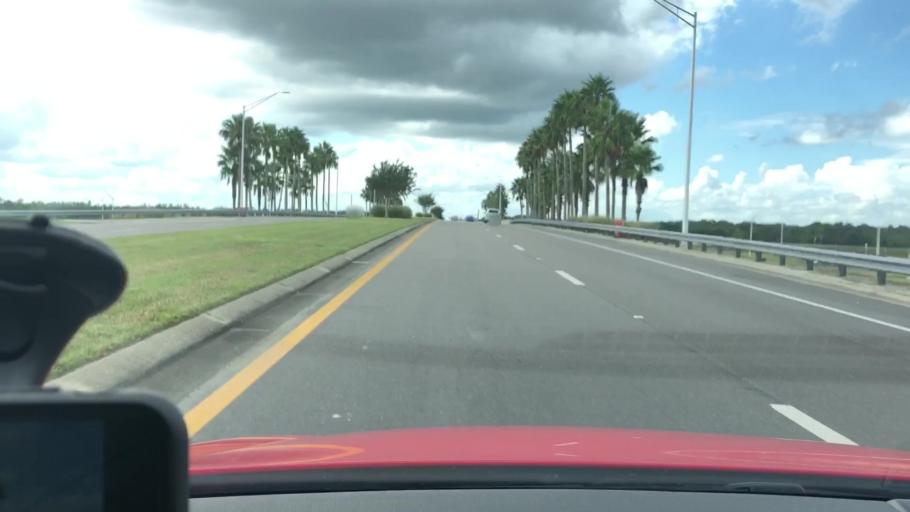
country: US
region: Florida
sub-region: Volusia County
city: Holly Hill
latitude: 29.2208
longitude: -81.1014
